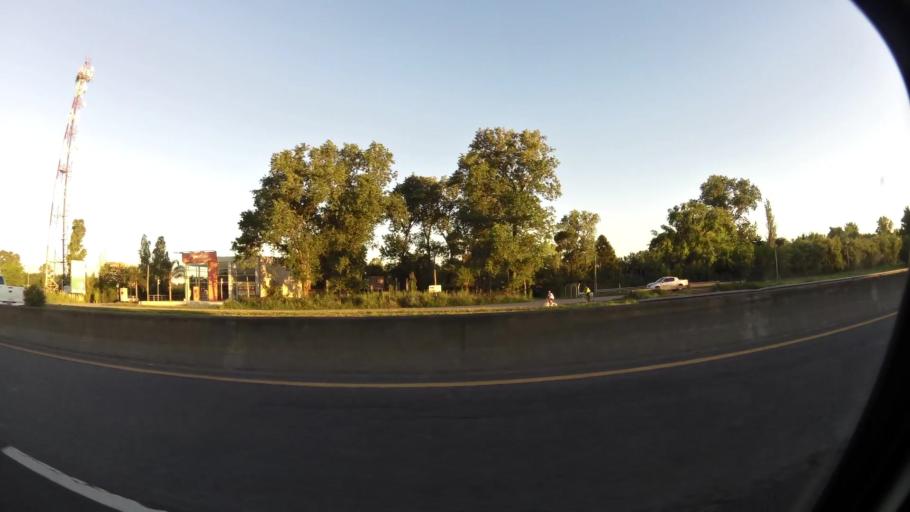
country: AR
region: Buenos Aires
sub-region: Partido de Quilmes
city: Quilmes
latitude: -34.8103
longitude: -58.1756
